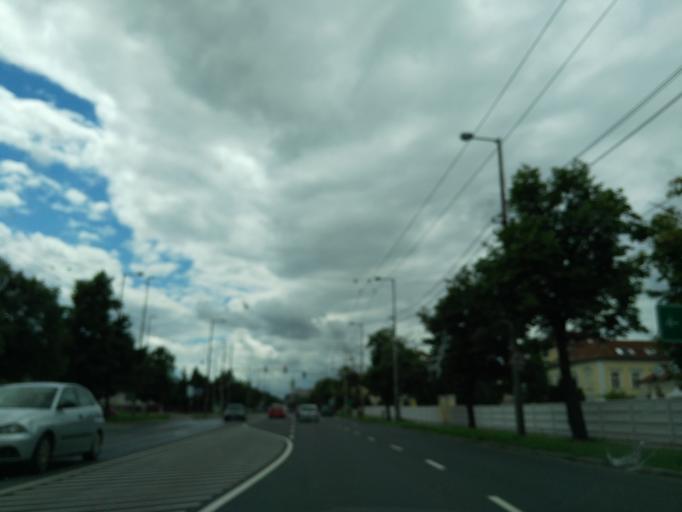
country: HU
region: Hajdu-Bihar
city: Debrecen
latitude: 47.5446
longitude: 21.6432
